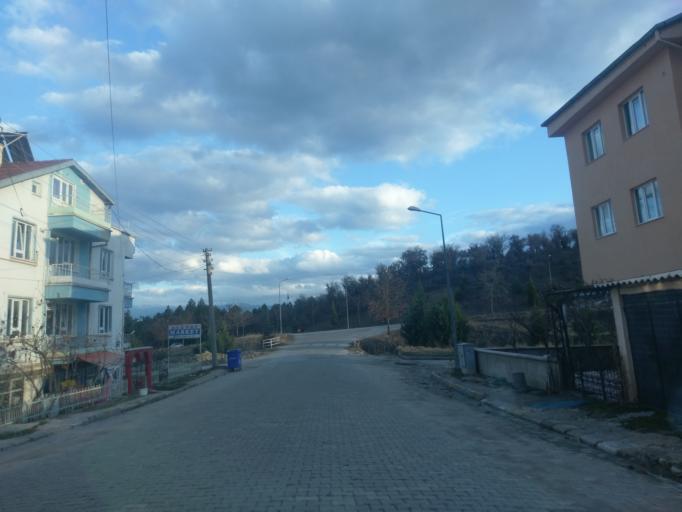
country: TR
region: Kuetahya
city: Gediz
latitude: 38.9883
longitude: 29.3865
